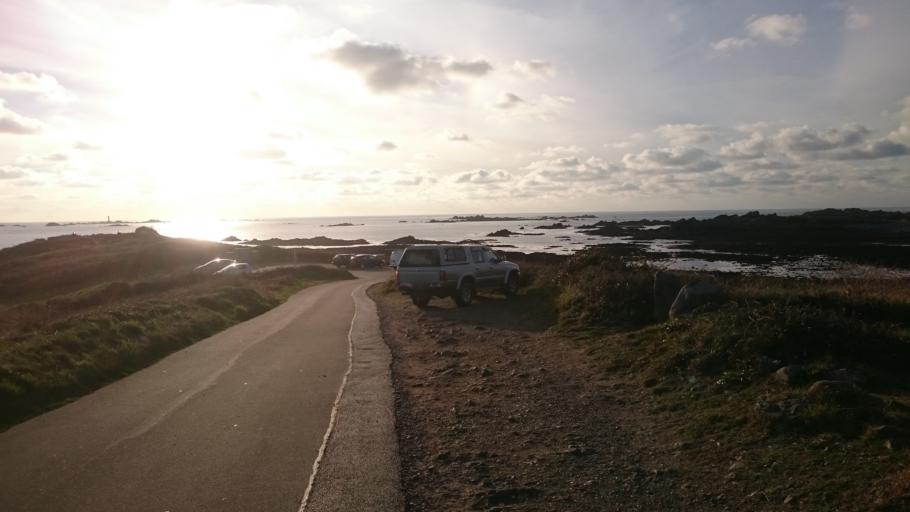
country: GG
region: St Peter Port
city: Saint Peter Port
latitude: 49.4567
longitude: -2.6572
